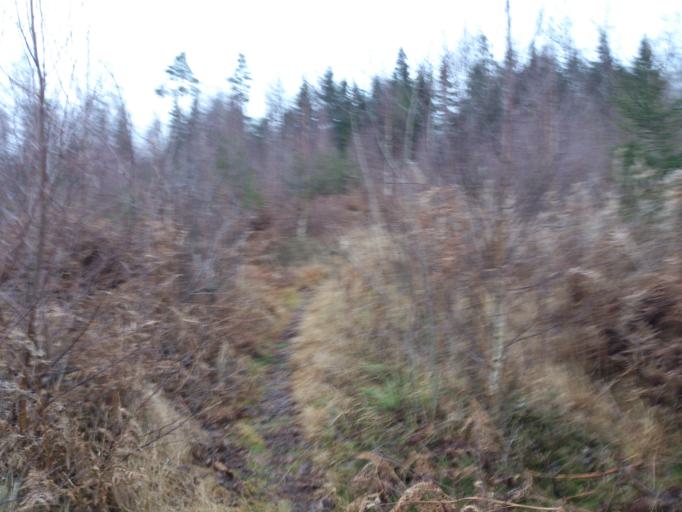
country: SE
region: Kronoberg
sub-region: Alvesta Kommun
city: Moheda
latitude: 57.0039
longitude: 14.5896
